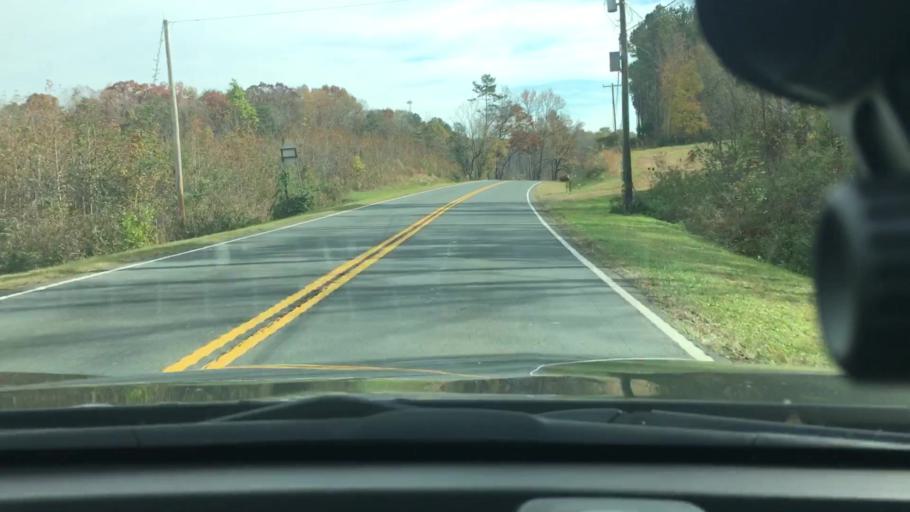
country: US
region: North Carolina
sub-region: Stanly County
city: Badin
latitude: 35.3170
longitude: -80.1099
